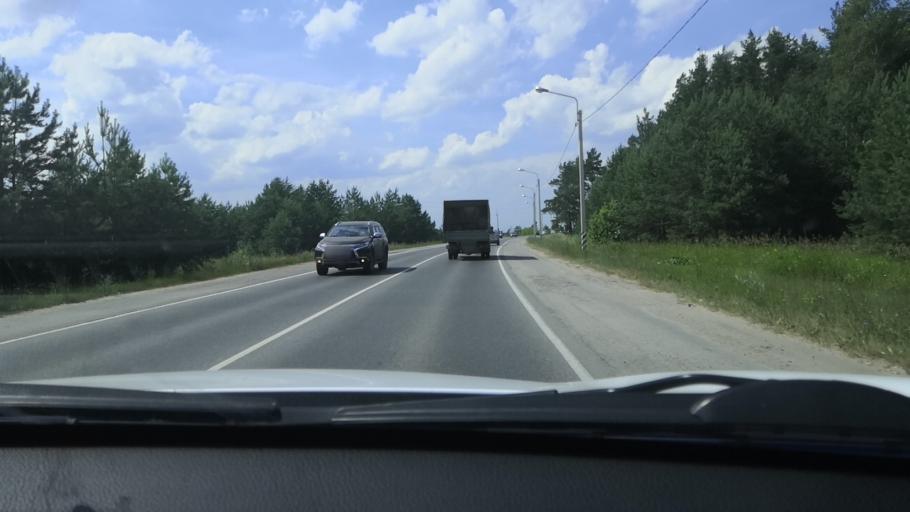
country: RU
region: Rjazan
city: Murmino
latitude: 54.6306
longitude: 39.9533
